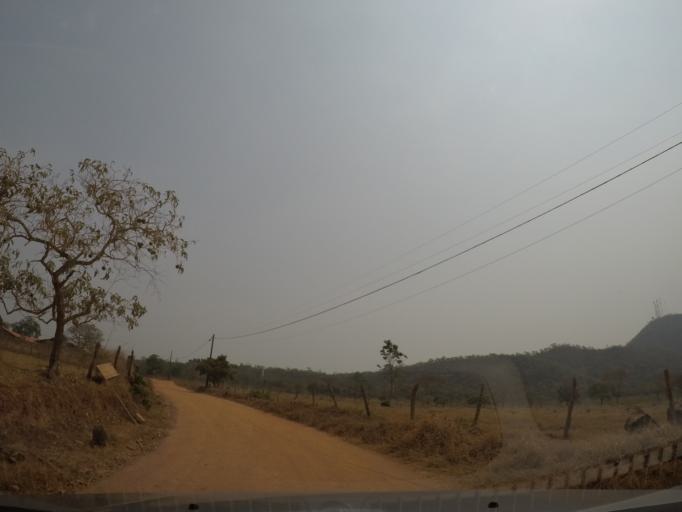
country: BR
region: Goias
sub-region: Pirenopolis
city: Pirenopolis
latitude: -15.8376
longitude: -48.9550
